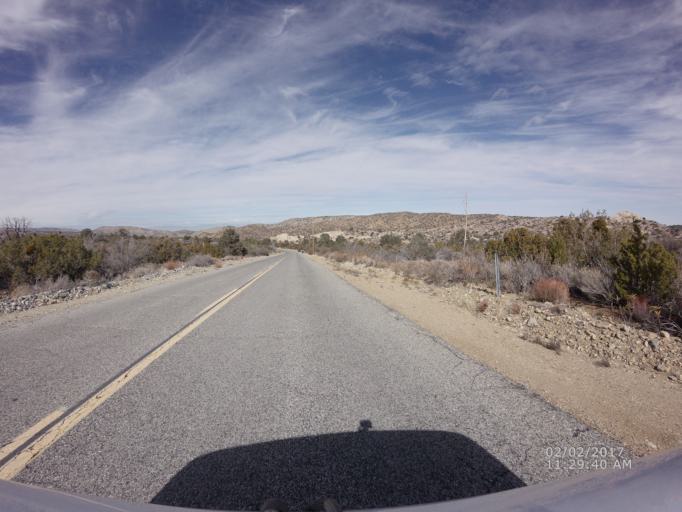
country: US
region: California
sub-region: Los Angeles County
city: Littlerock
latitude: 34.4271
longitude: -117.8700
